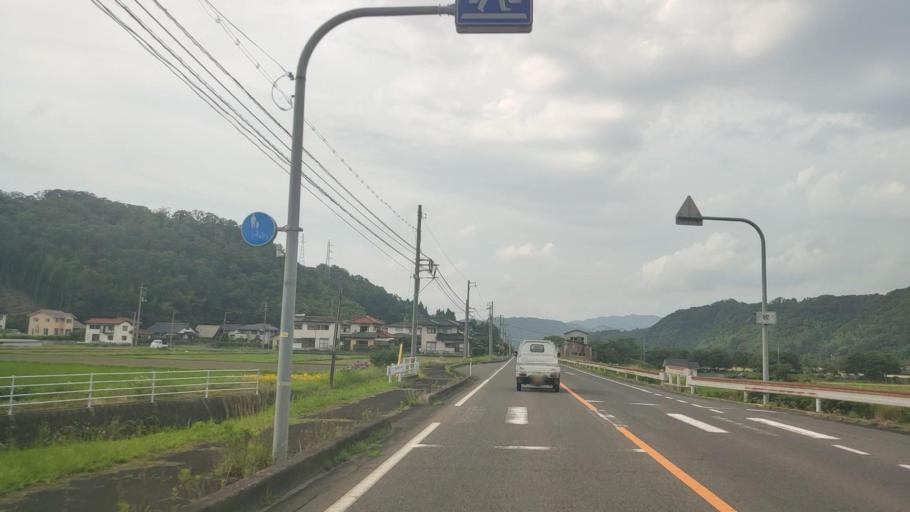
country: JP
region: Tottori
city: Kurayoshi
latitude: 35.3851
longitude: 133.8561
